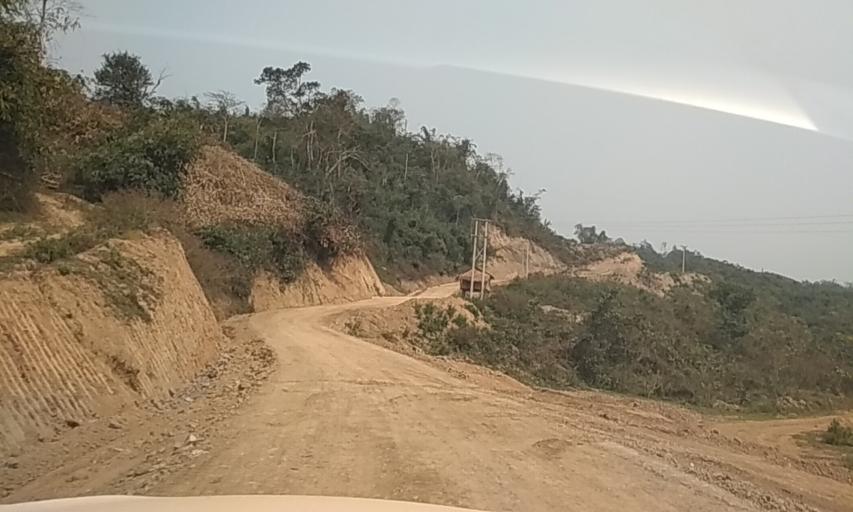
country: VN
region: Huyen Dien Bien
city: Dien Bien Phu
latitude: 21.4360
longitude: 102.7669
